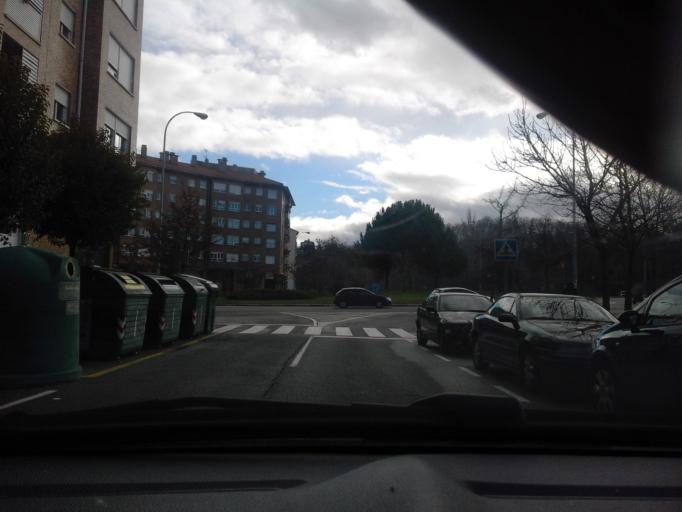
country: ES
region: Navarre
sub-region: Provincia de Navarra
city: Primer Ensanche
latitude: 42.8233
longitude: -1.6543
